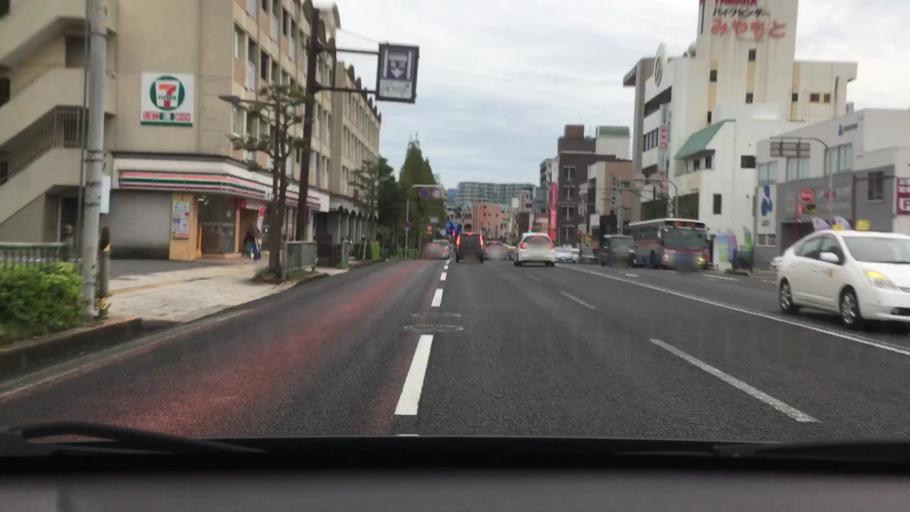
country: JP
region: Nagasaki
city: Nagasaki-shi
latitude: 32.7754
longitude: 129.8622
